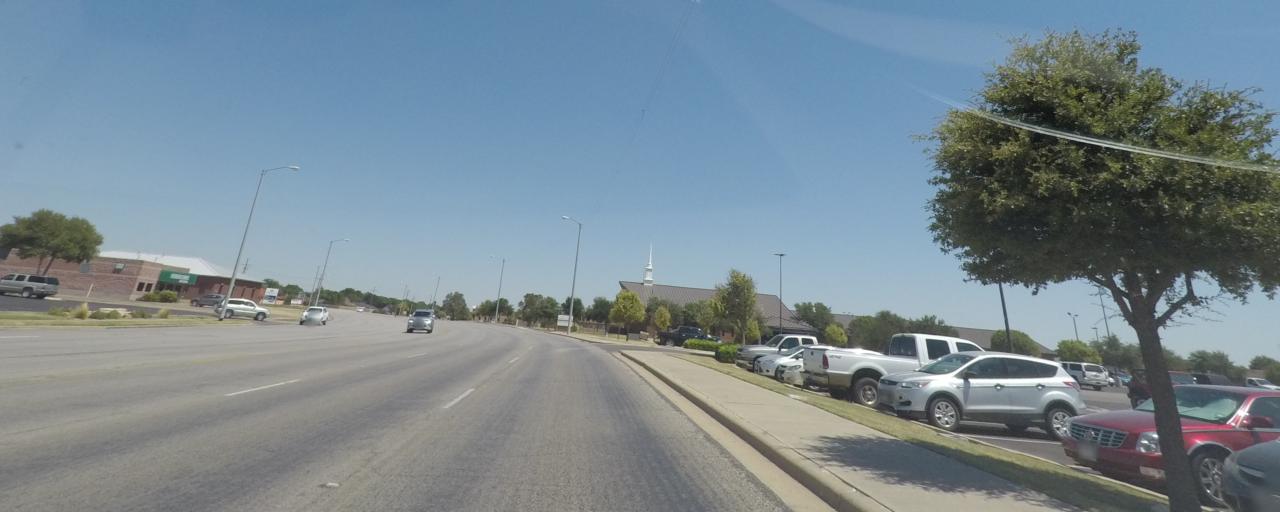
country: US
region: Texas
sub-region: Lubbock County
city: Lubbock
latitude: 33.5044
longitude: -101.9030
